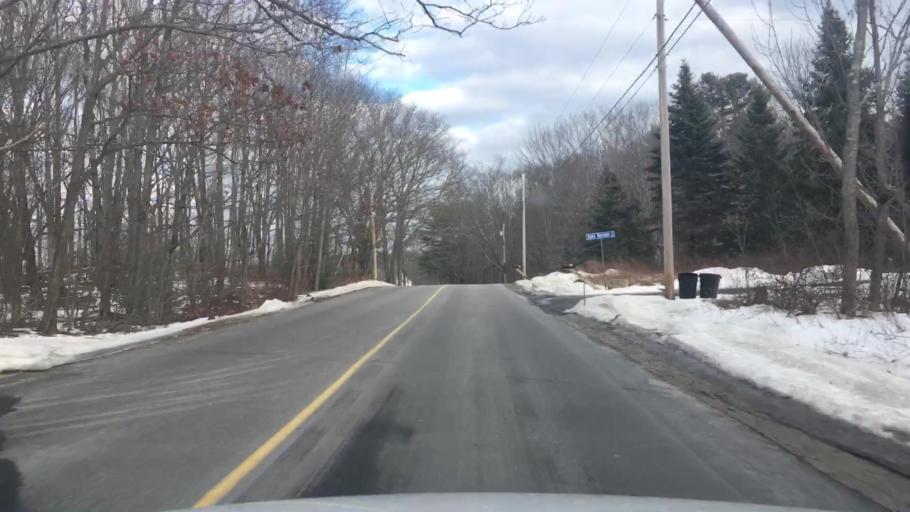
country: US
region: Maine
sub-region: York County
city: Arundel
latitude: 43.4114
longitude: -70.4762
